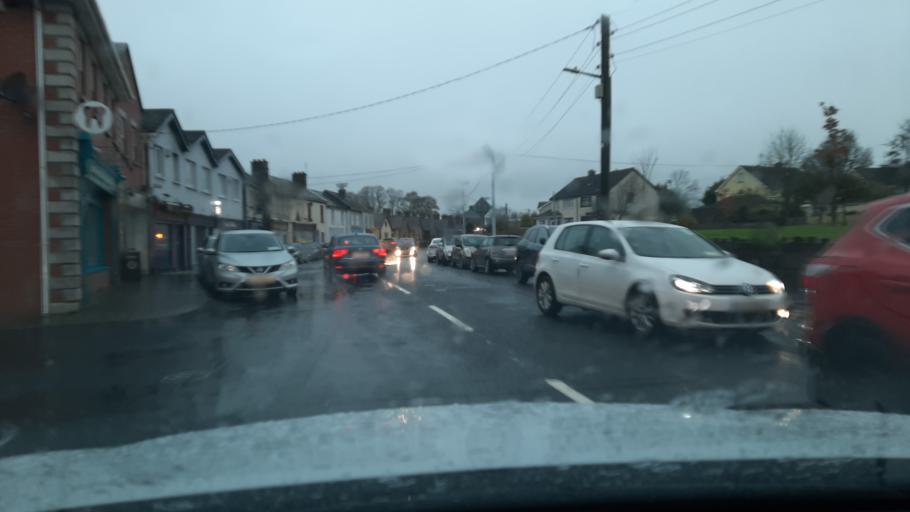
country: IE
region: Leinster
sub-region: Kildare
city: Kildare
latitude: 53.1598
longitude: -6.9092
